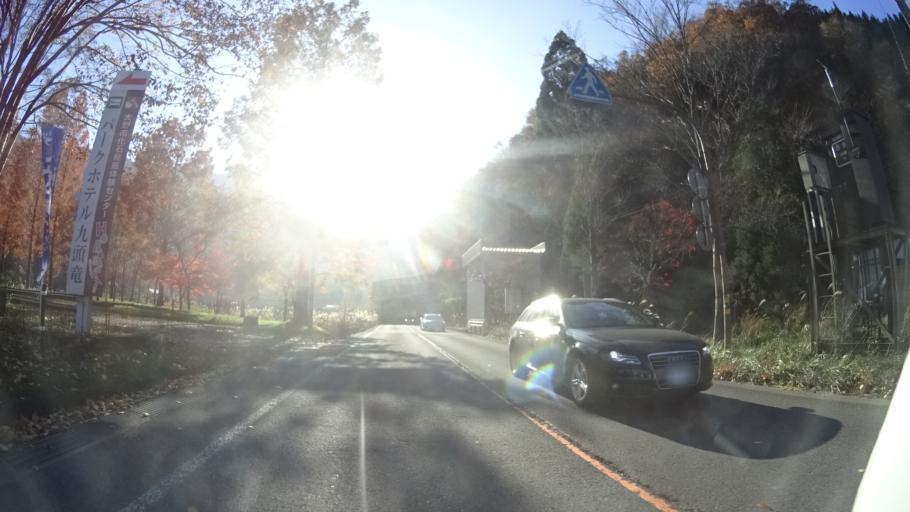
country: JP
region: Fukui
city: Ono
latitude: 35.9017
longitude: 136.6571
